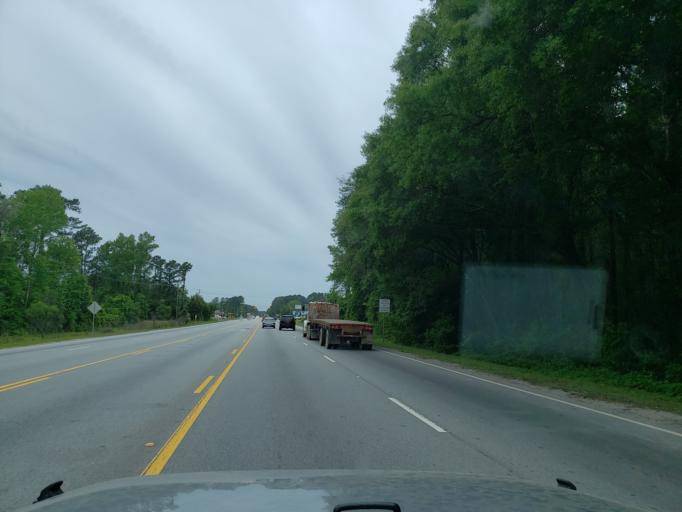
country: US
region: Georgia
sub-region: Chatham County
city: Garden City
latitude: 32.0930
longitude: -81.1983
